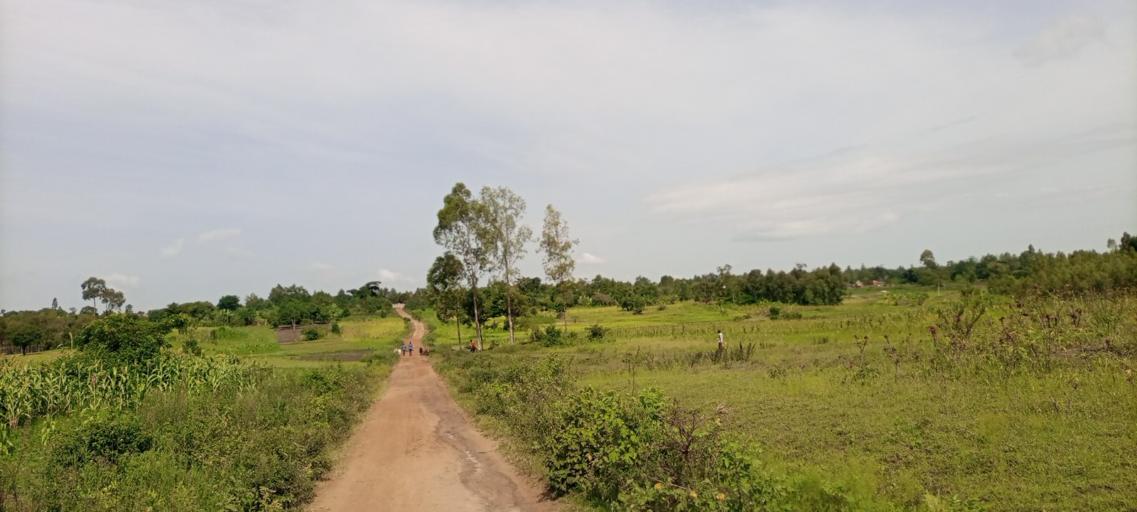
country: UG
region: Eastern Region
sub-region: Mbale District
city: Mbale
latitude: 1.1284
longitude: 34.0355
